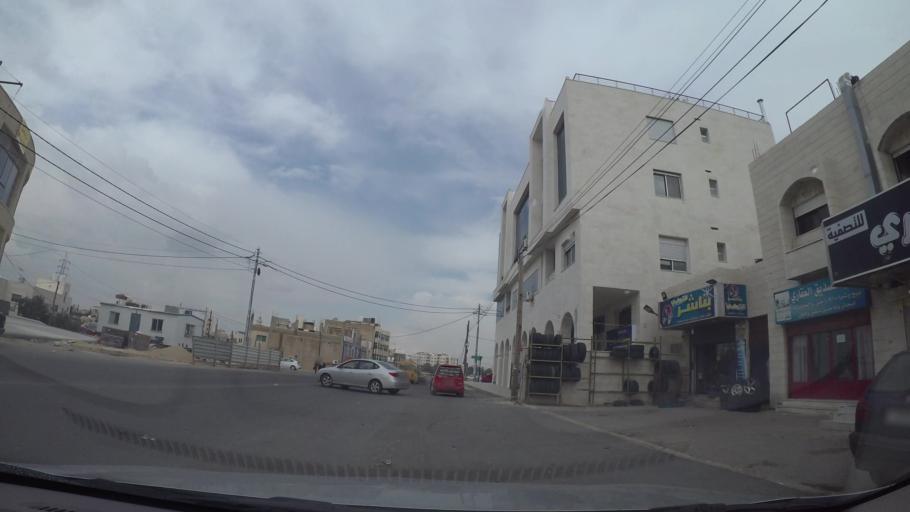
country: JO
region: Amman
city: Umm as Summaq
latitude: 31.8961
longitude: 35.8646
